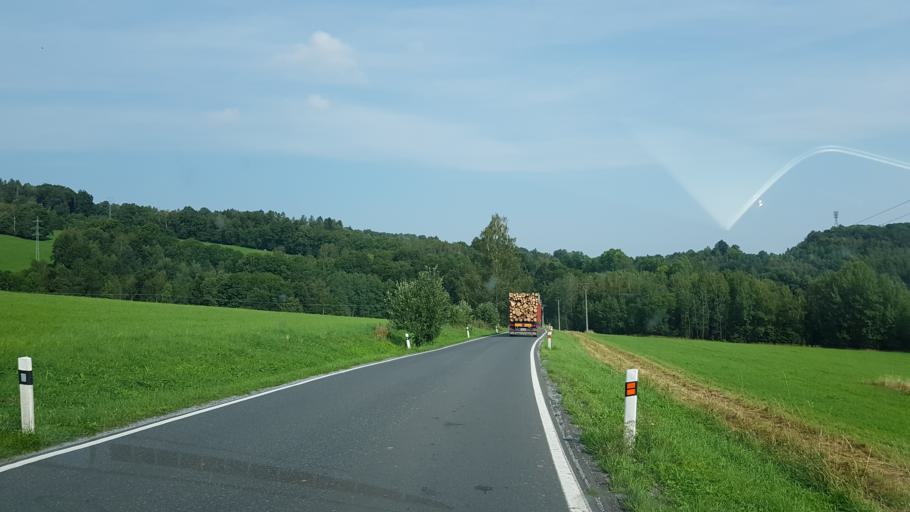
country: CZ
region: Olomoucky
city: Zlate Hory
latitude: 50.2363
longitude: 17.3420
